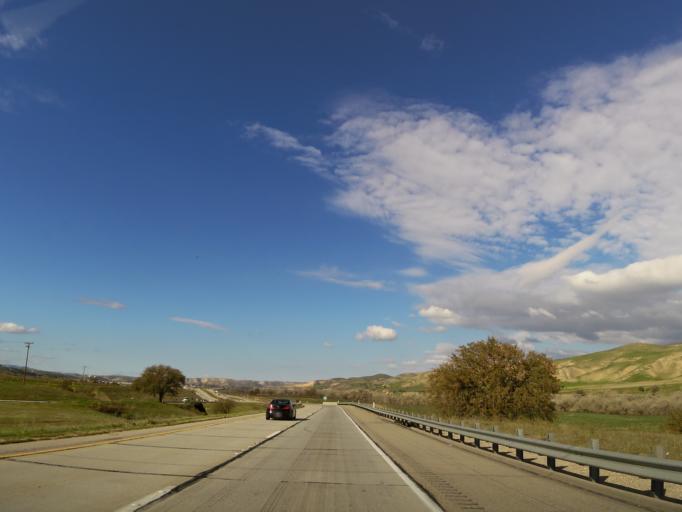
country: US
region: California
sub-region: San Luis Obispo County
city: San Miguel
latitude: 35.7691
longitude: -120.7039
